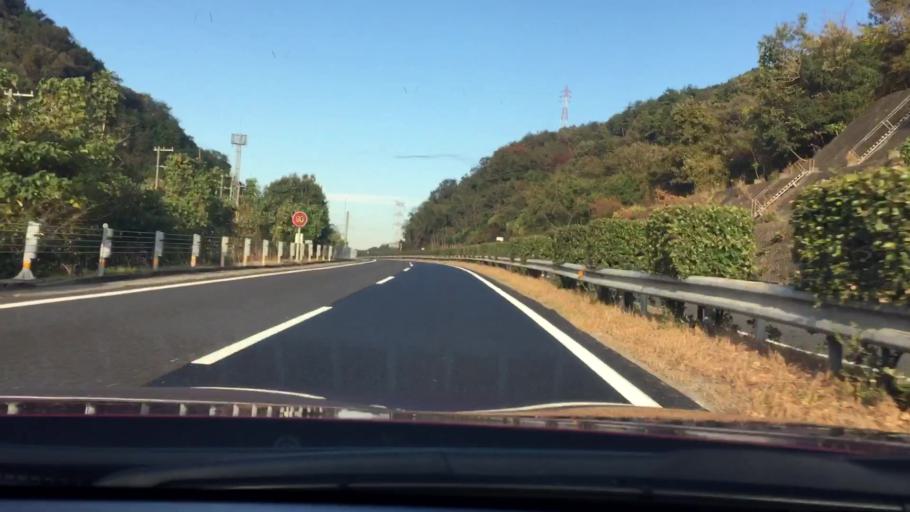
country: JP
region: Hyogo
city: Yamazakicho-nakabirose
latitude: 34.9798
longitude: 134.6234
